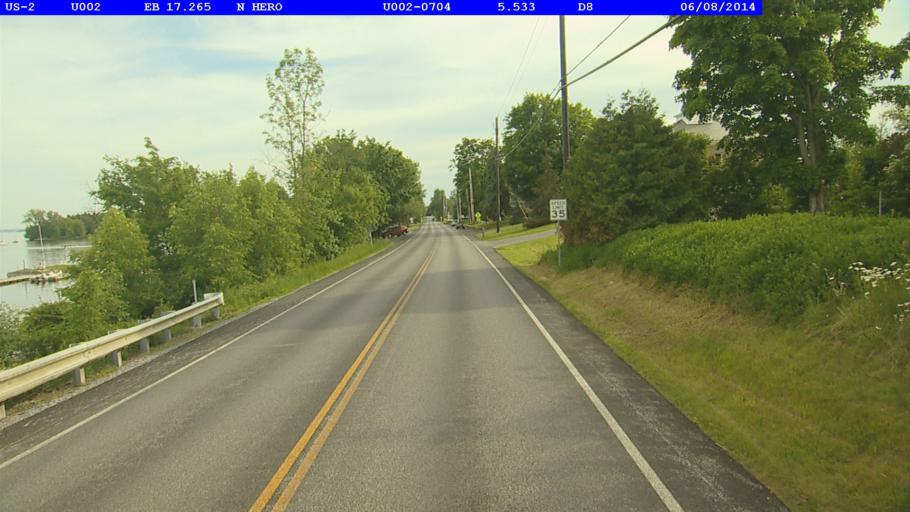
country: US
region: Vermont
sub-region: Grand Isle County
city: North Hero
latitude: 44.8193
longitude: -73.2890
